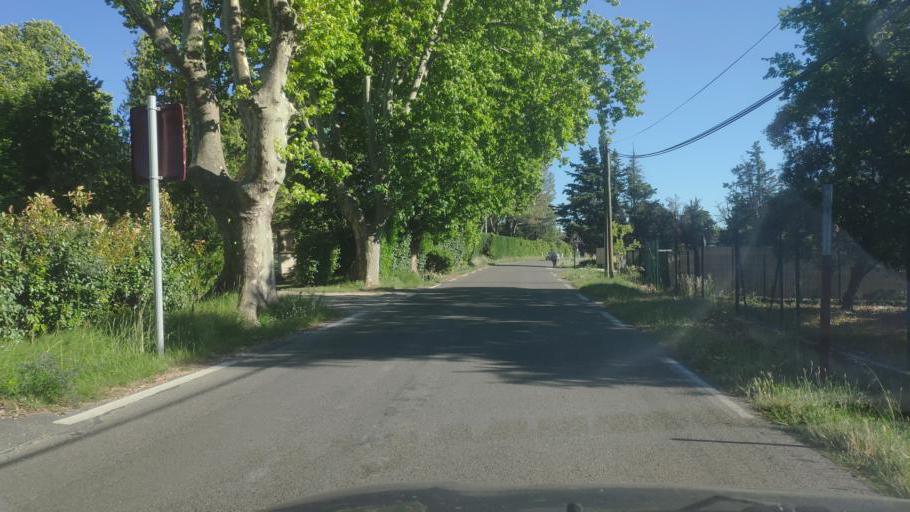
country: FR
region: Provence-Alpes-Cote d'Azur
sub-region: Departement du Vaucluse
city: Aubignan
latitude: 44.0925
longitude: 5.0256
